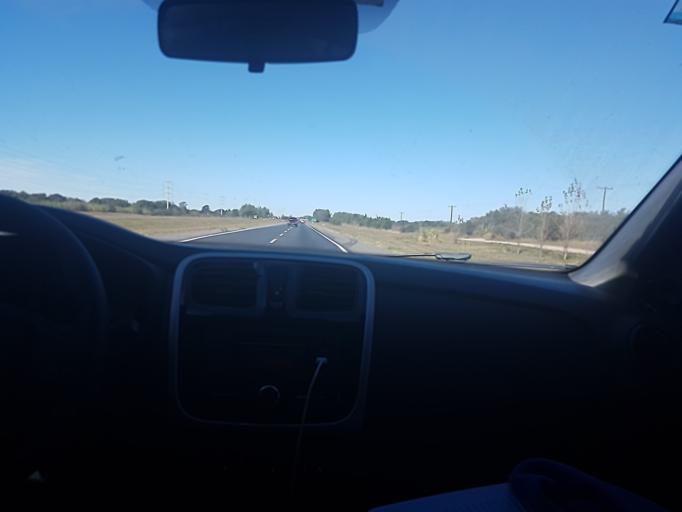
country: AR
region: Cordoba
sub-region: Departamento de Rio Segundo
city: Rio Segundo
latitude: -31.6368
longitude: -63.8697
